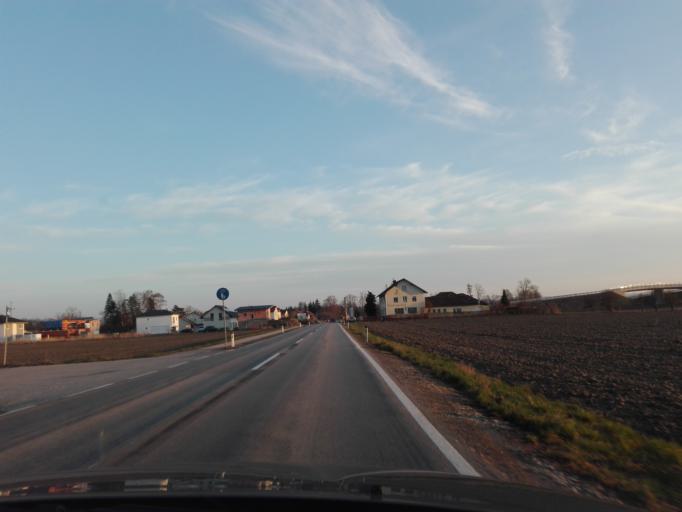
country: AT
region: Upper Austria
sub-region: Politischer Bezirk Urfahr-Umgebung
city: Feldkirchen an der Donau
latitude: 48.3280
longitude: 14.0103
